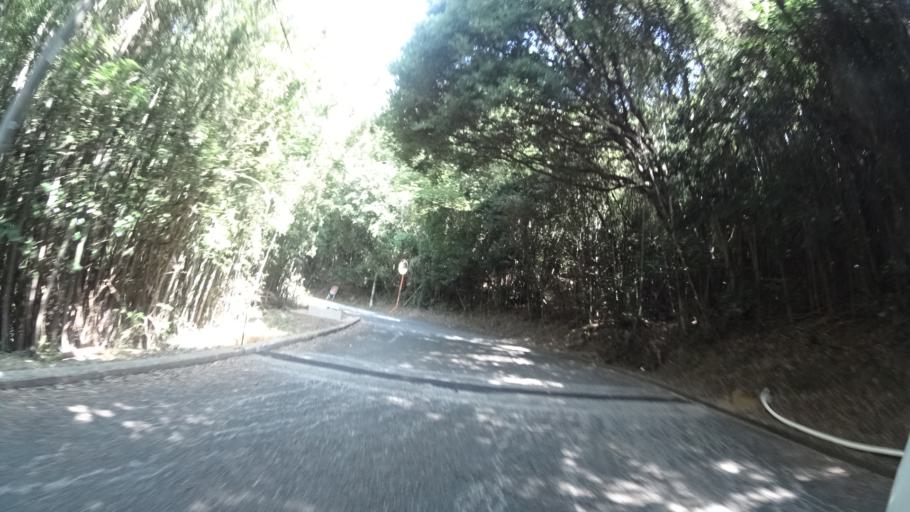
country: JP
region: Yamaguchi
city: Shimonoseki
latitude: 34.1077
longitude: 130.8683
